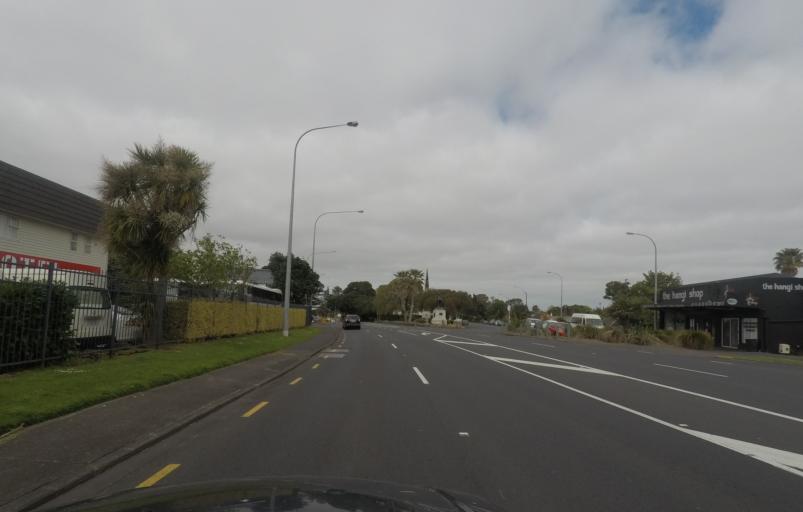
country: NZ
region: Auckland
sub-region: Auckland
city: Mangere
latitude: -36.9492
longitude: 174.8454
